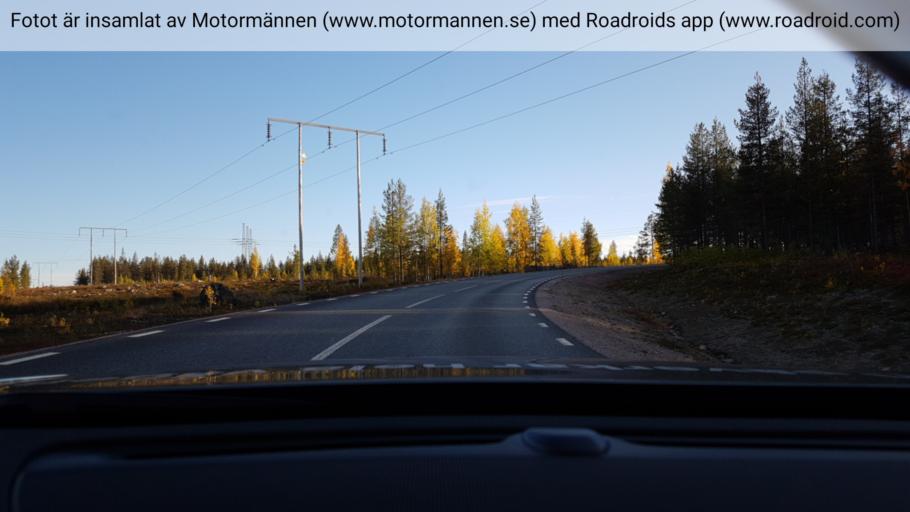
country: SE
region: Norrbotten
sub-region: Jokkmokks Kommun
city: Jokkmokk
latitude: 66.8036
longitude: 19.8753
